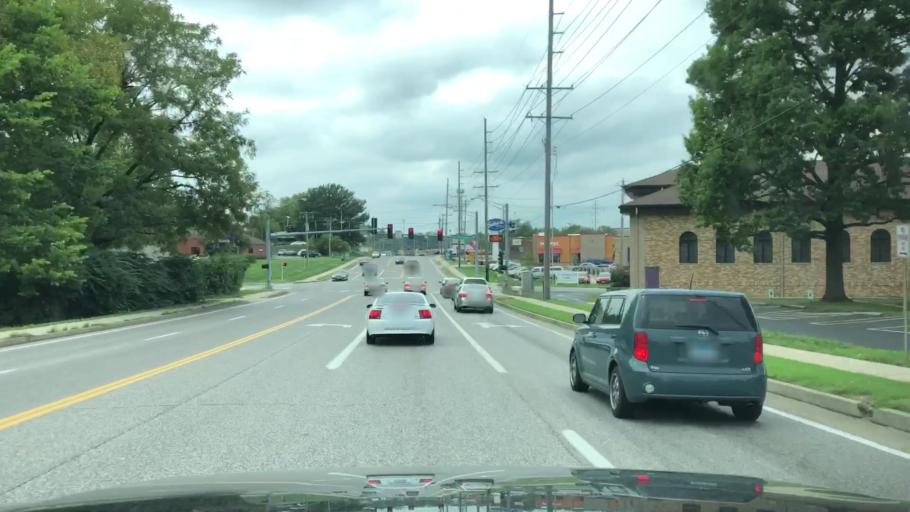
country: US
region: Missouri
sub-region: Saint Louis County
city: Florissant
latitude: 38.7991
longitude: -90.3272
